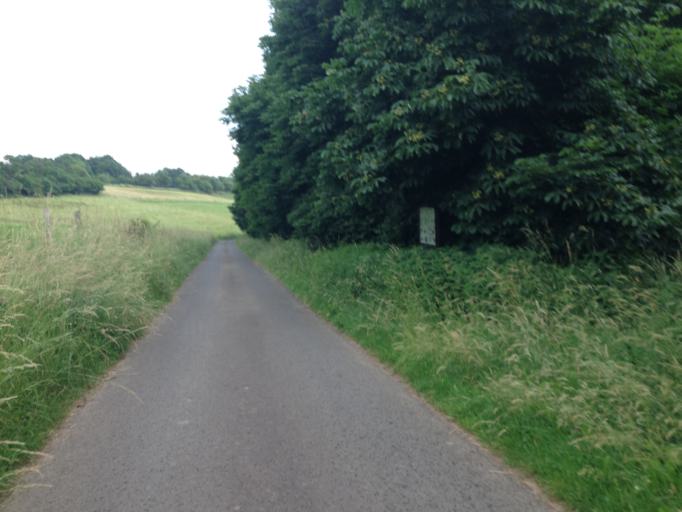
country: DE
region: Hesse
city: Wetter
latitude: 50.8574
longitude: 8.7324
